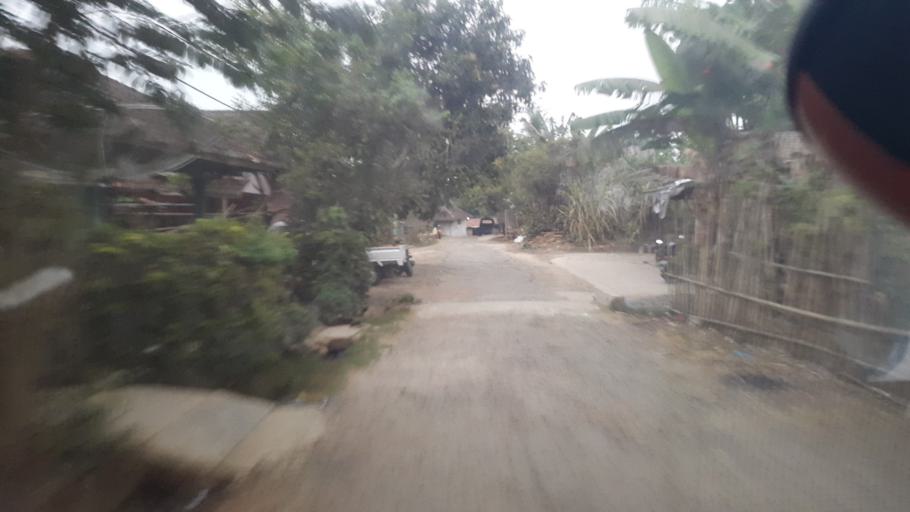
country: ID
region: West Java
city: Cikujang
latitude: -7.3690
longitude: 106.5706
